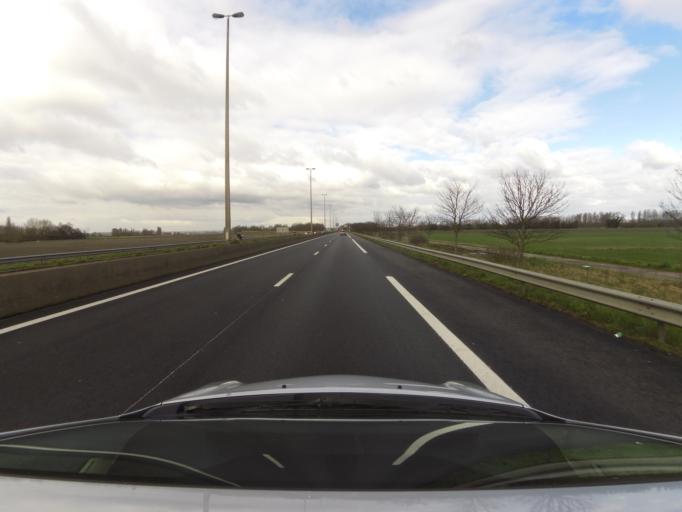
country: FR
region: Nord-Pas-de-Calais
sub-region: Departement du Pas-de-Calais
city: Marck
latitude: 50.9353
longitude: 1.9797
